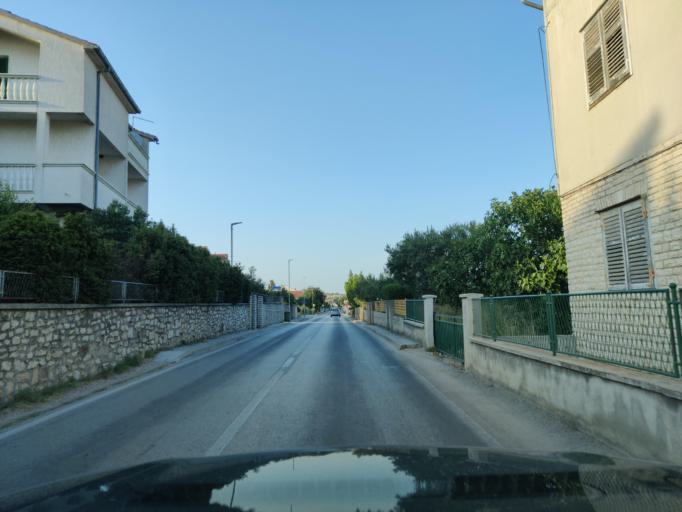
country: HR
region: Sibensko-Kniniska
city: Vodice
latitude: 43.7581
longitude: 15.7682
